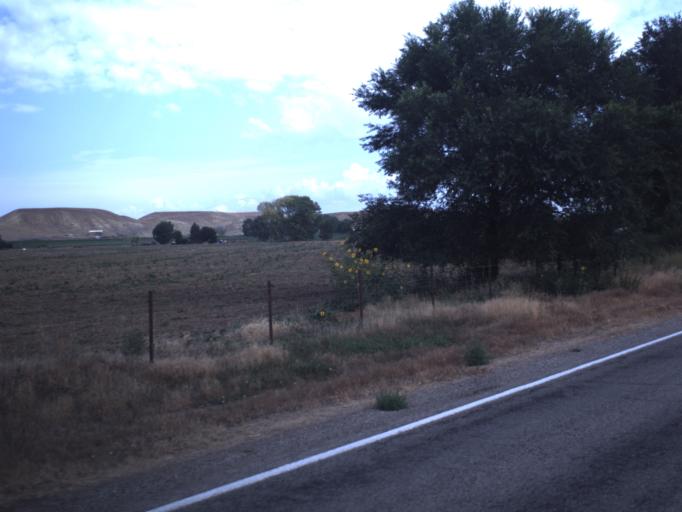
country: US
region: Utah
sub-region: Uintah County
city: Naples
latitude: 40.3955
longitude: -109.3460
